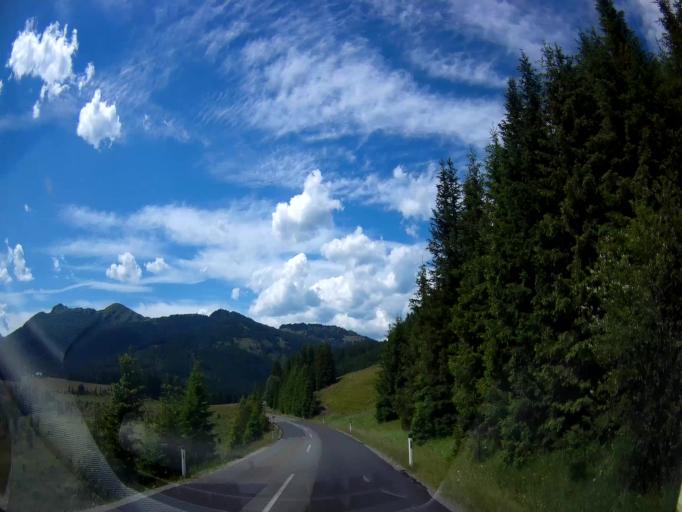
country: AT
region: Styria
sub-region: Politischer Bezirk Murau
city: Stadl an der Mur
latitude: 46.9671
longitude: 14.0193
